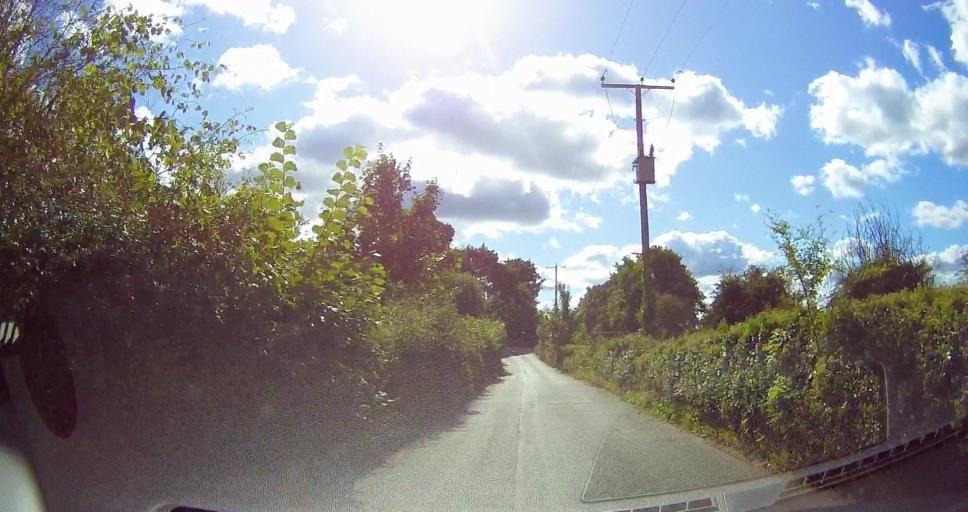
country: GB
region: England
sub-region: Staffordshire
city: Stone
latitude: 52.9160
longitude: -2.1637
